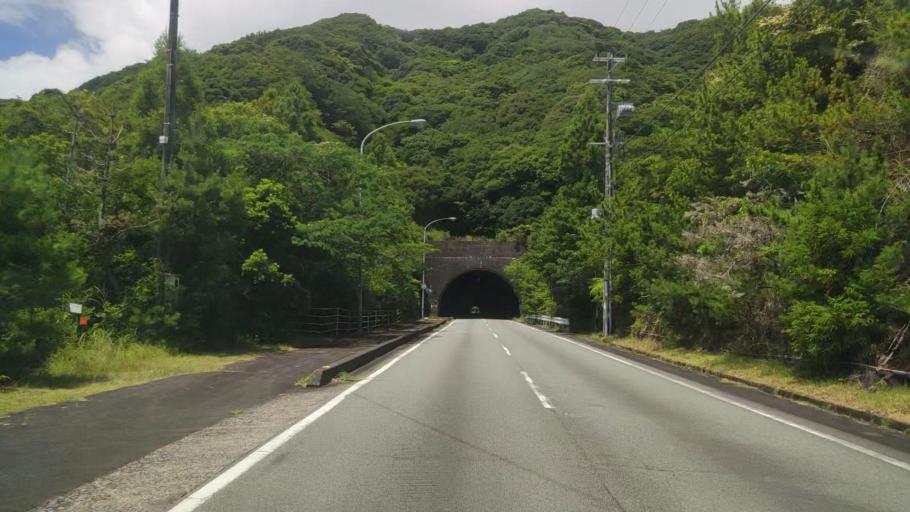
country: JP
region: Mie
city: Ise
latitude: 34.2952
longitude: 136.6267
